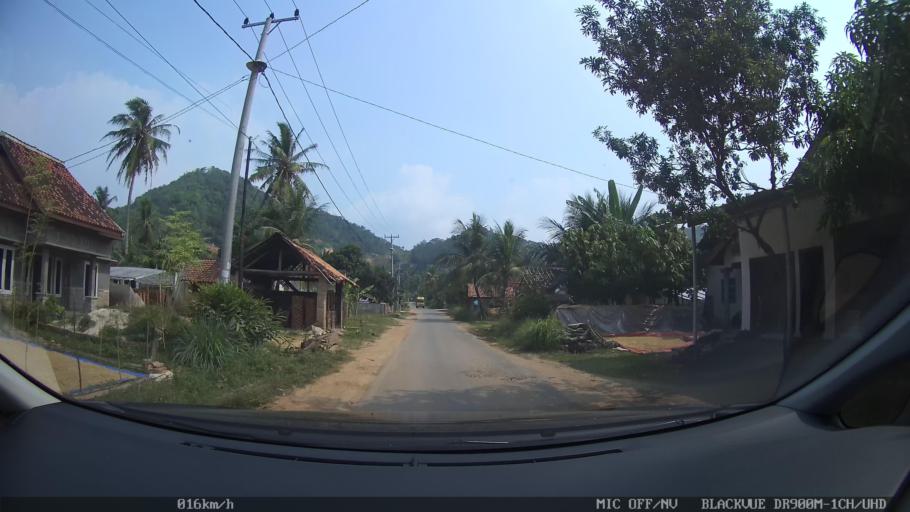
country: ID
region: Lampung
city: Pringsewu
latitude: -5.3795
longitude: 105.0001
